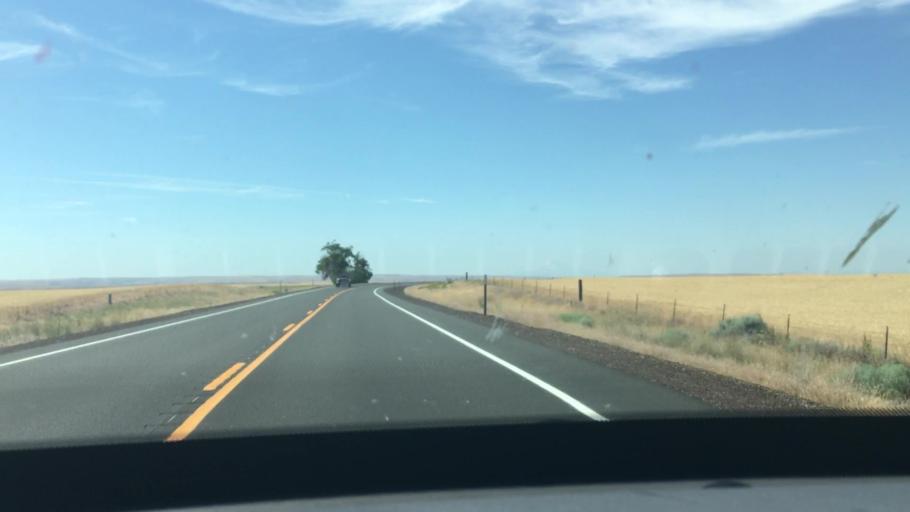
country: US
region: Oregon
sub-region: Sherman County
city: Moro
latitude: 45.3040
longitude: -120.7661
